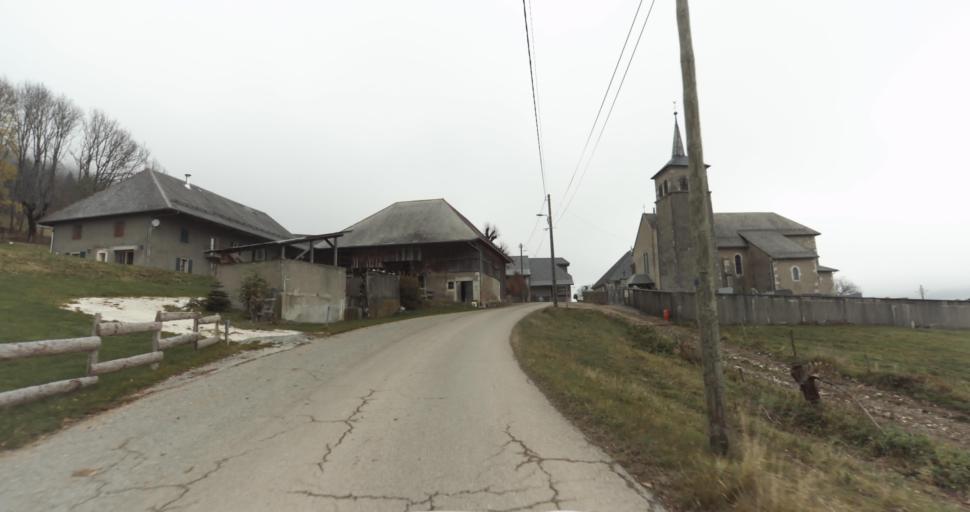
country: FR
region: Rhone-Alpes
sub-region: Departement de la Haute-Savoie
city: Gruffy
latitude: 45.7683
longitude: 6.1220
